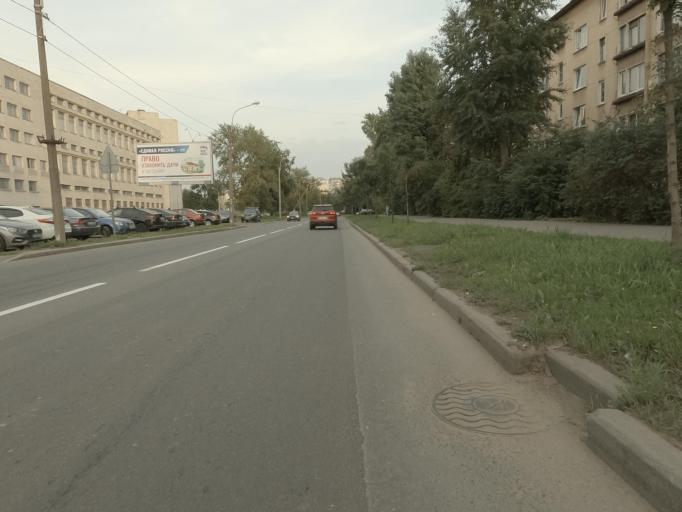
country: RU
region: St.-Petersburg
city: Dachnoye
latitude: 59.8550
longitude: 30.2644
